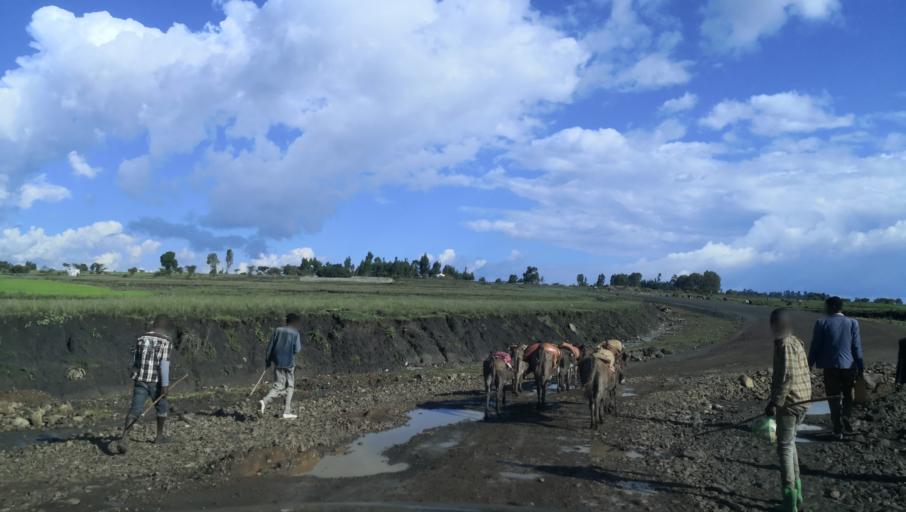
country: ET
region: Oromiya
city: Tulu Bolo
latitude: 8.5783
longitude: 38.2406
